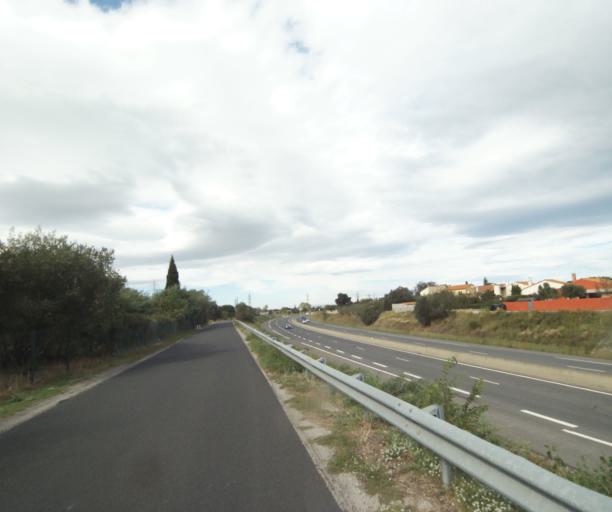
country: FR
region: Languedoc-Roussillon
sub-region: Departement des Pyrenees-Orientales
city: Argelers
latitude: 42.5456
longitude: 3.0078
